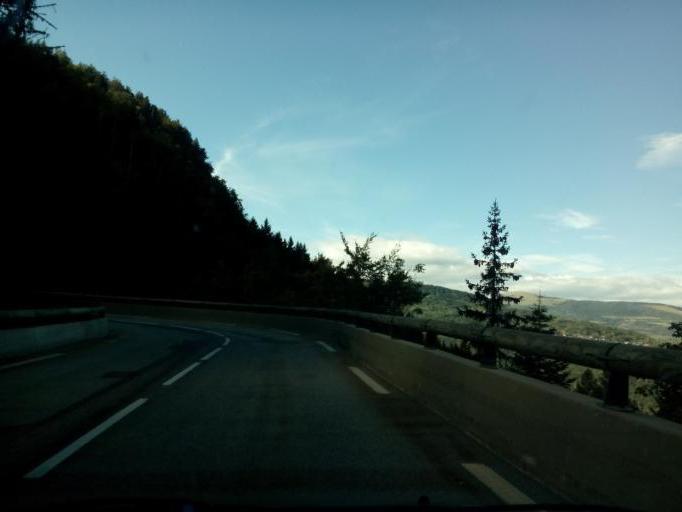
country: FR
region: Rhone-Alpes
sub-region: Departement de l'Isere
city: Vaulnaveys-le-Bas
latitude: 45.0453
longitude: 5.8407
